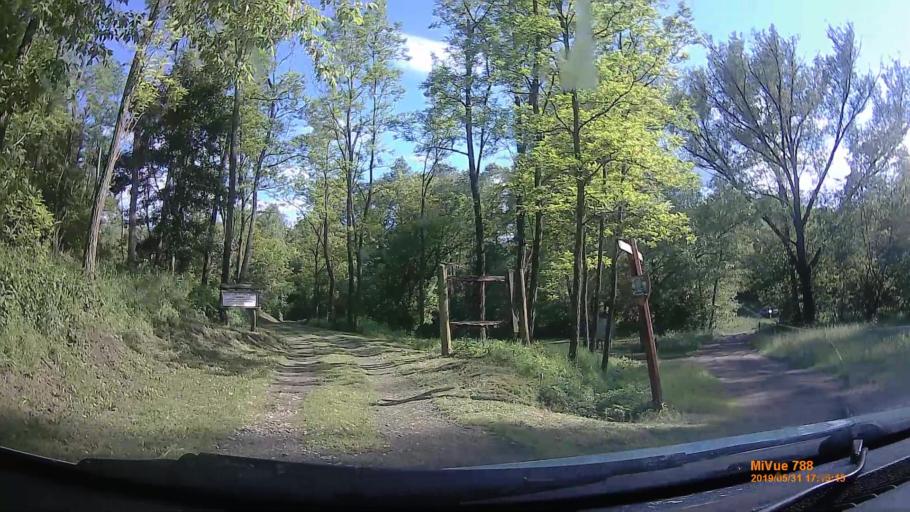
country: HU
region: Nograd
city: Nagyoroszi
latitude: 48.0298
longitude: 19.0460
